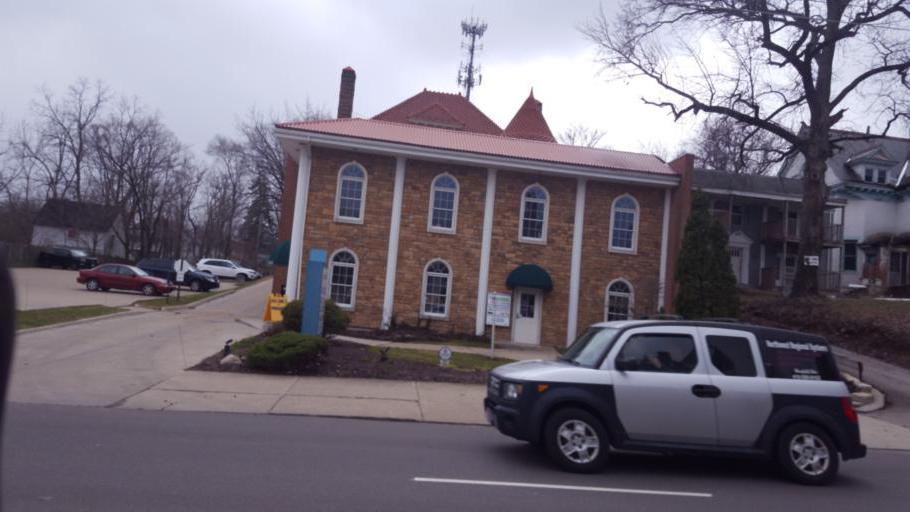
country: US
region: Ohio
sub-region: Richland County
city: Mansfield
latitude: 40.7589
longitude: -82.5285
